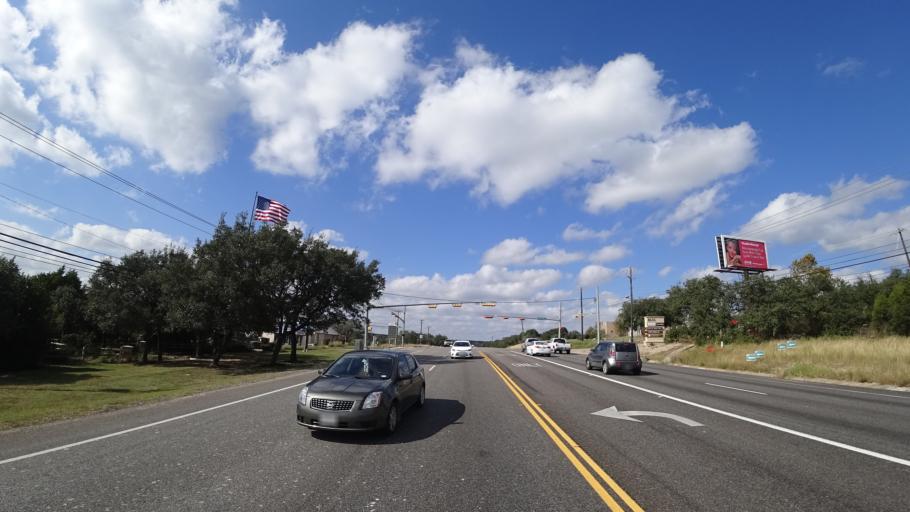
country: US
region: Texas
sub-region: Travis County
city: Barton Creek
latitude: 30.2496
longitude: -97.8938
